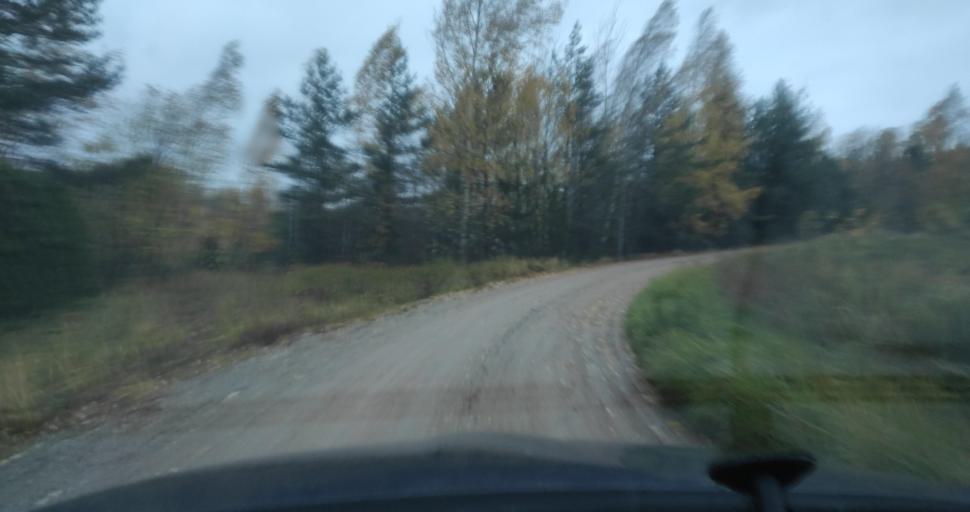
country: LV
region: Kuldigas Rajons
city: Kuldiga
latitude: 56.9071
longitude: 21.9301
